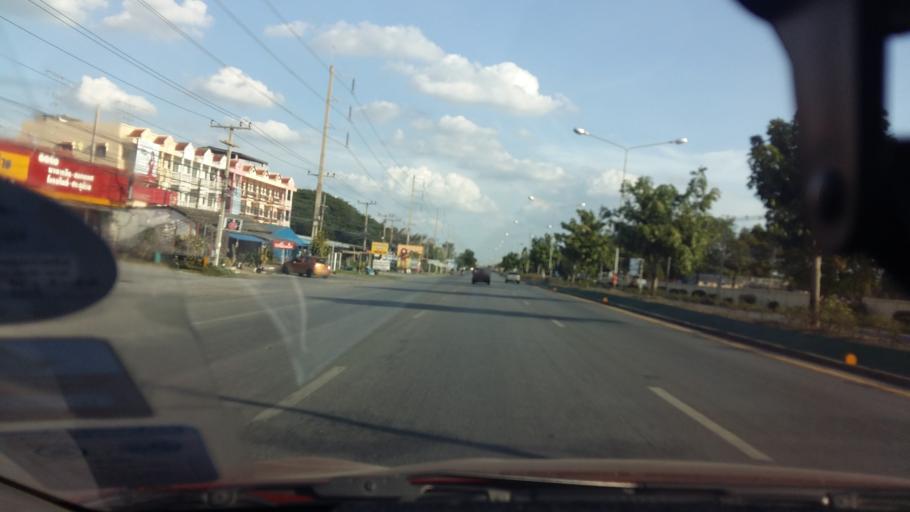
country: TH
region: Lop Buri
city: Lop Buri
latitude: 14.8387
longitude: 100.6445
